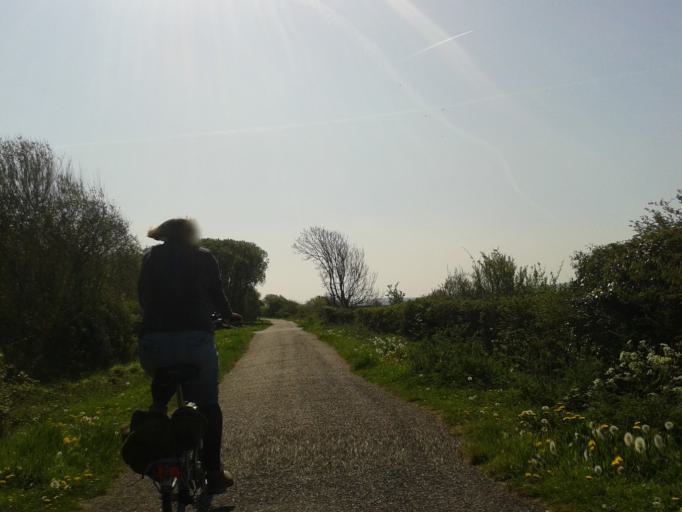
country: GB
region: England
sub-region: Devon
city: Braunton
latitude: 51.0999
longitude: -4.1609
